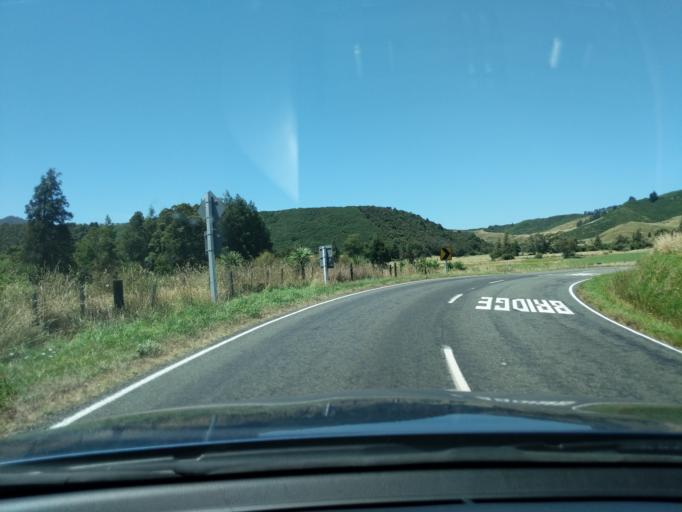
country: NZ
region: Tasman
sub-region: Tasman District
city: Takaka
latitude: -40.7414
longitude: 172.5678
